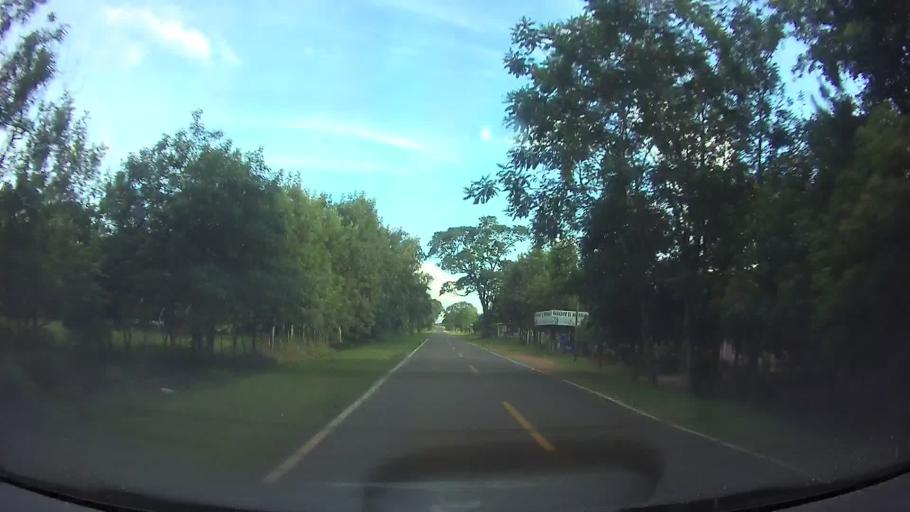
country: PY
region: Paraguari
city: Acahay
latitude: -25.9450
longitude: -57.0962
